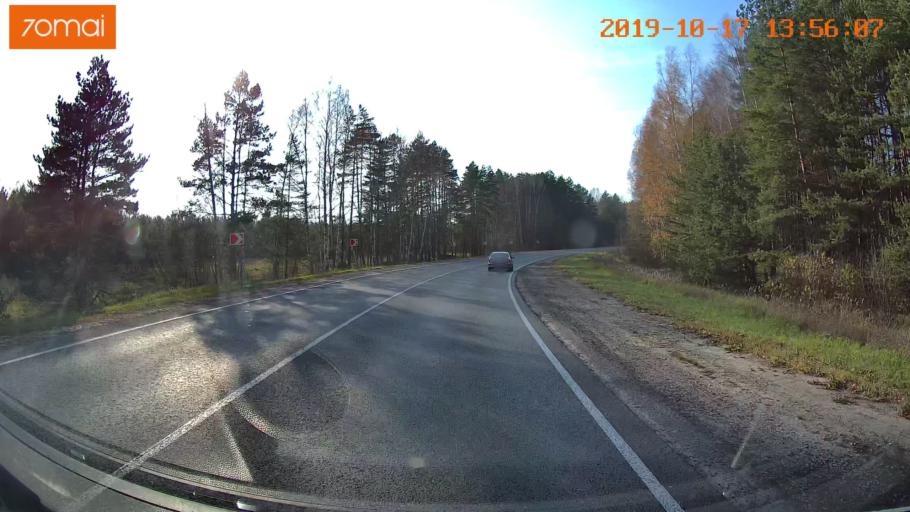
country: RU
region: Rjazan
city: Spas-Klepiki
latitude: 55.1514
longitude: 40.2735
